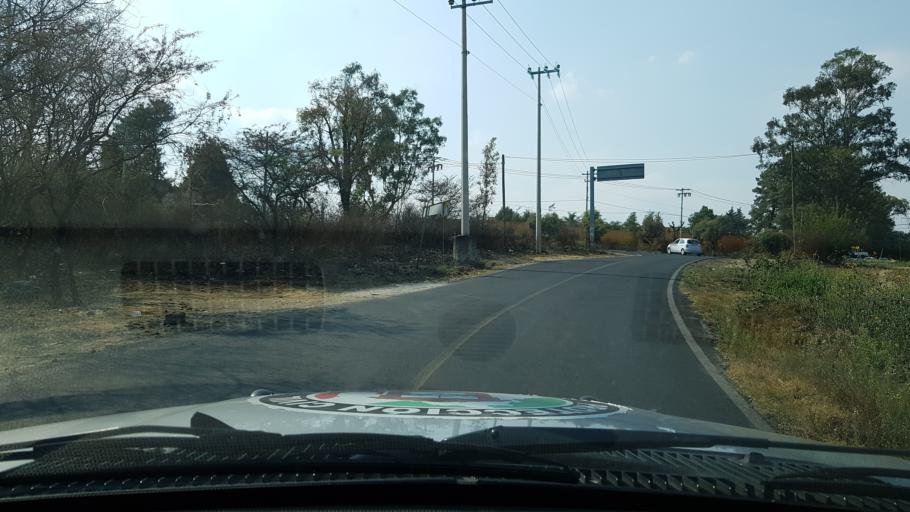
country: MX
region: Mexico
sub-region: Tepetlixpa
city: Nepantla de Sor Juana Ines de la Cruz
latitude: 18.9911
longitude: -98.8249
